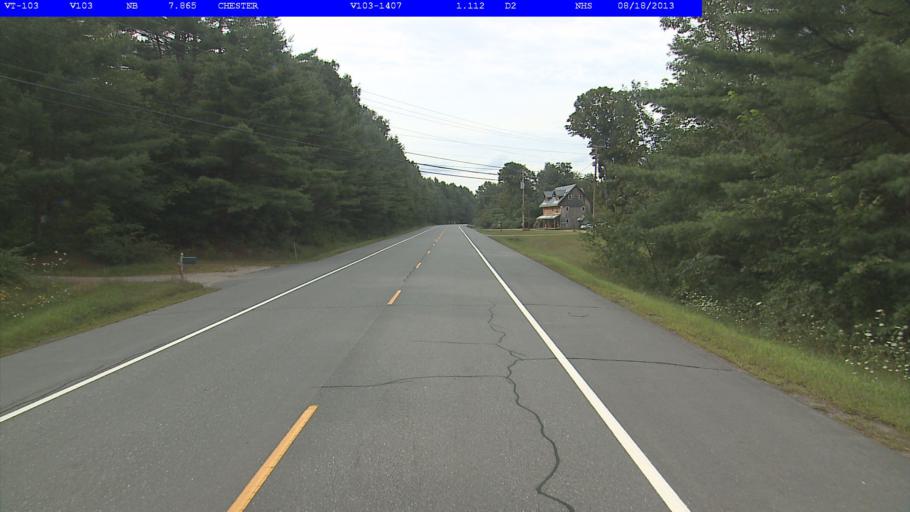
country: US
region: Vermont
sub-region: Windsor County
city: Chester
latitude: 43.2450
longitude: -72.5703
